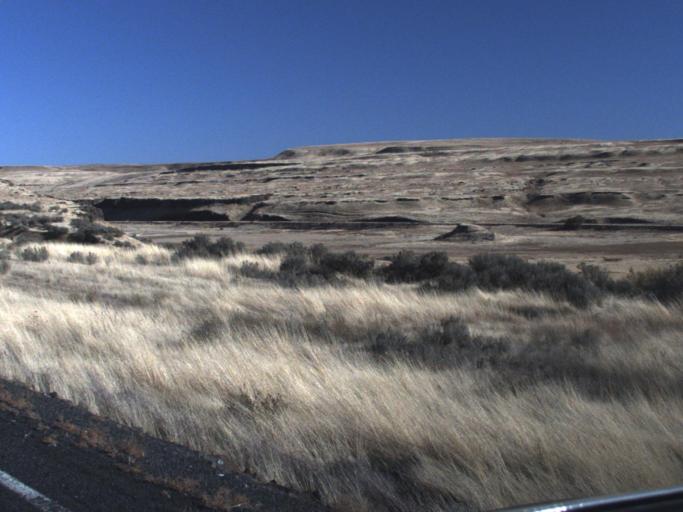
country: US
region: Washington
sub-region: Franklin County
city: Connell
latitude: 46.6467
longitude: -118.5415
